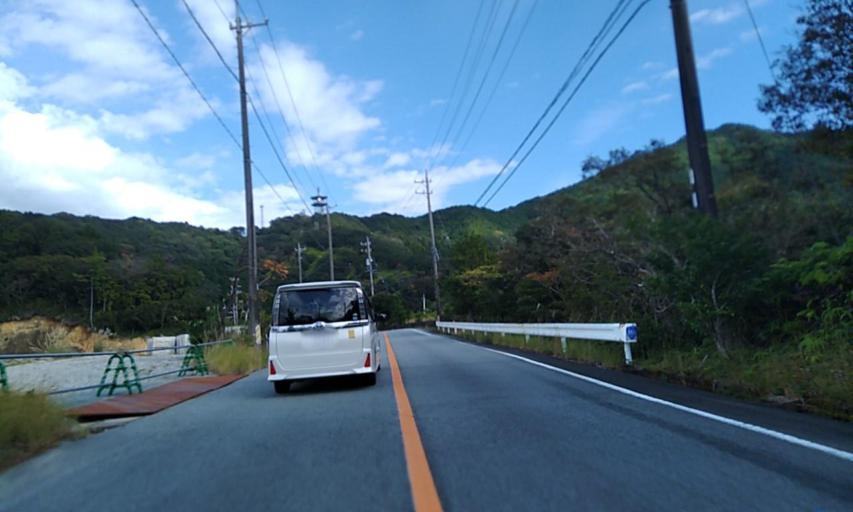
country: JP
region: Mie
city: Owase
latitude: 34.2141
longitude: 136.3660
